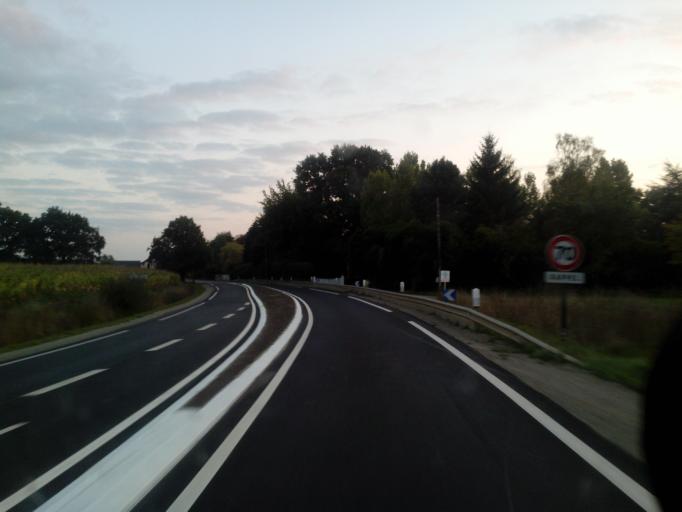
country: FR
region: Brittany
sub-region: Departement d'Ille-et-Vilaine
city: Bedee
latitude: 48.1721
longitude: -1.9442
